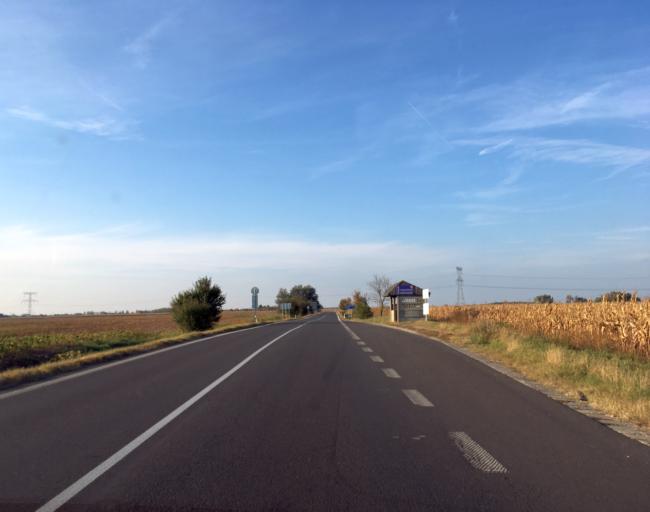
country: SK
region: Nitriansky
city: Surany
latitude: 48.0627
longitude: 18.0991
